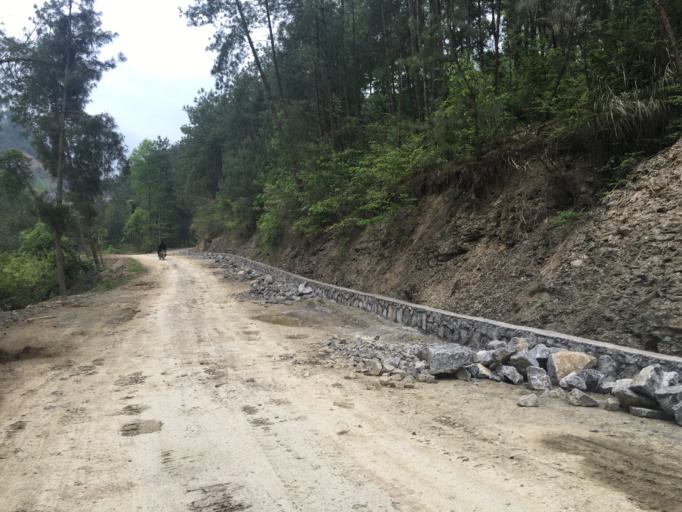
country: CN
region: Guizhou Sheng
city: Changbao
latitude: 28.2073
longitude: 108.2847
